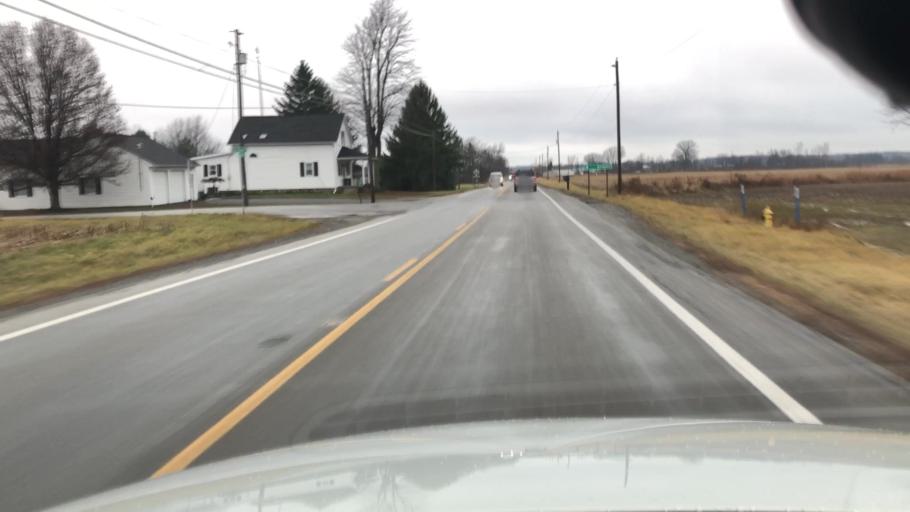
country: US
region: Ohio
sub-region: Allen County
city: Lima
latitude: 40.7037
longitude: -83.9983
